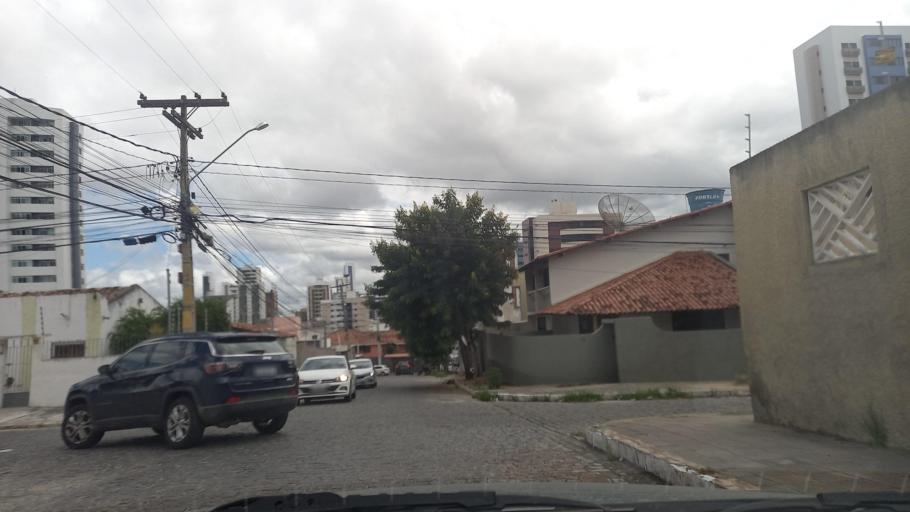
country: BR
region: Pernambuco
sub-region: Caruaru
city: Caruaru
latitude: -8.2687
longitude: -35.9670
